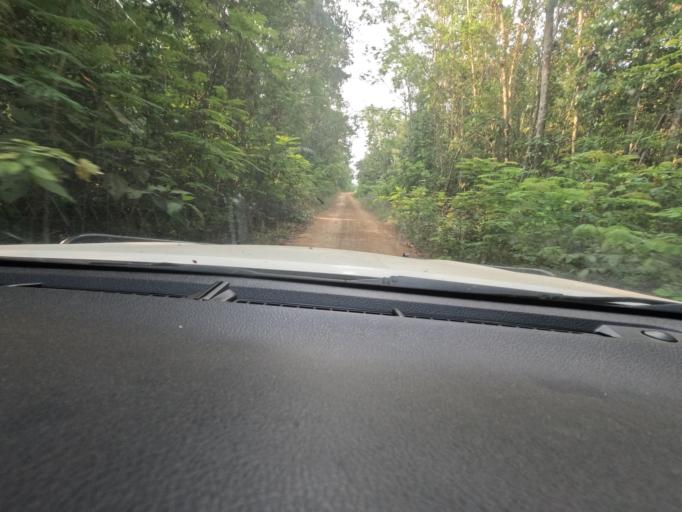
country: BR
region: Rondonia
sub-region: Porto Velho
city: Porto Velho
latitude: -8.6499
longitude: -63.1560
